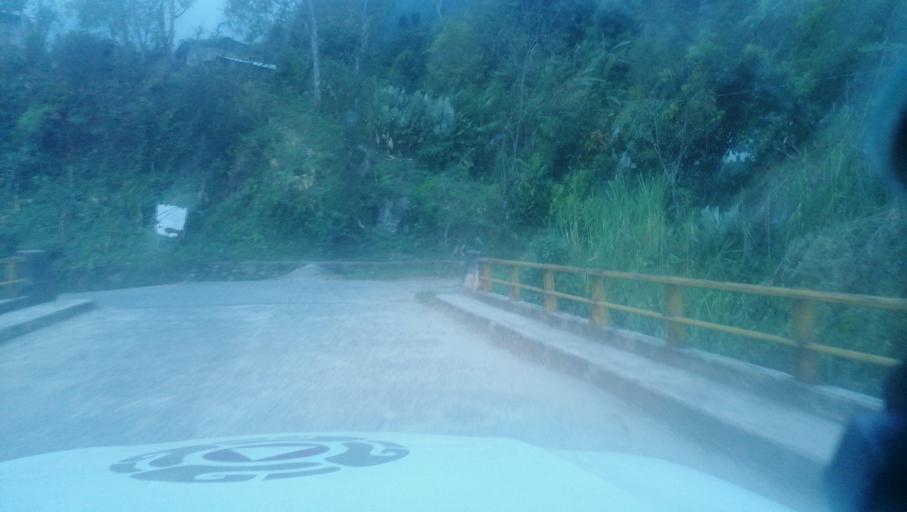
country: MX
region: Chiapas
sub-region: Cacahoatan
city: Benito Juarez
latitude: 15.1214
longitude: -92.2095
